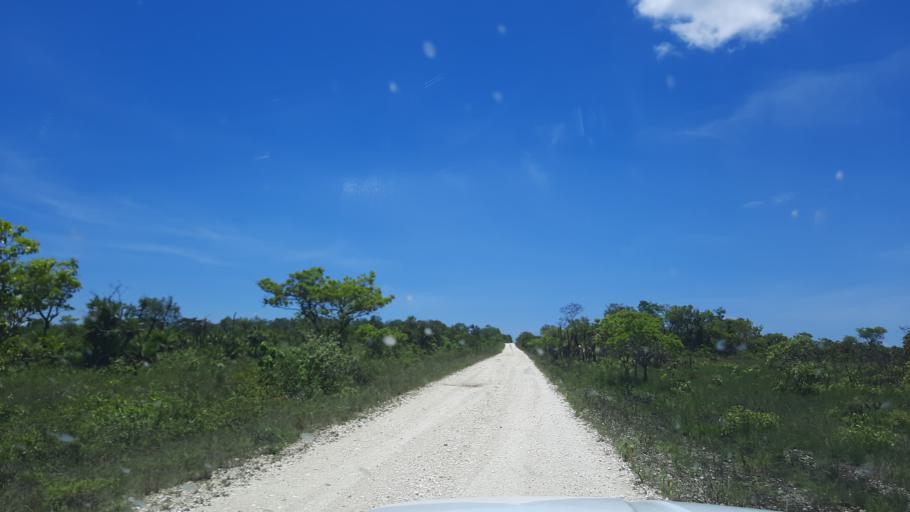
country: BZ
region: Belize
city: Belize City
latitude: 17.3952
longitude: -88.4870
